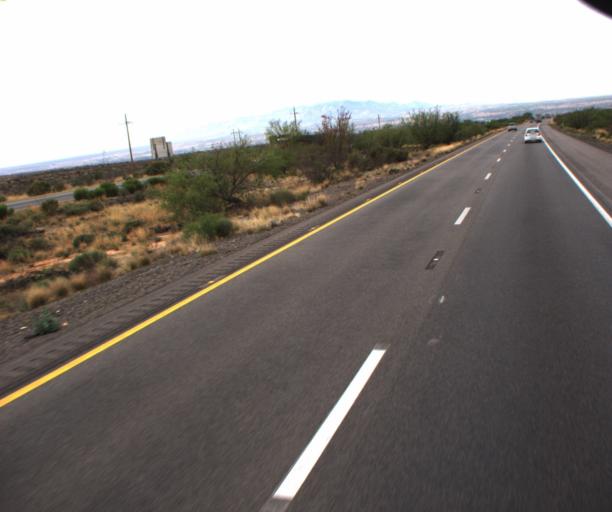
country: US
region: Arizona
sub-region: Cochise County
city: Saint David
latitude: 31.9861
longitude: -110.1949
